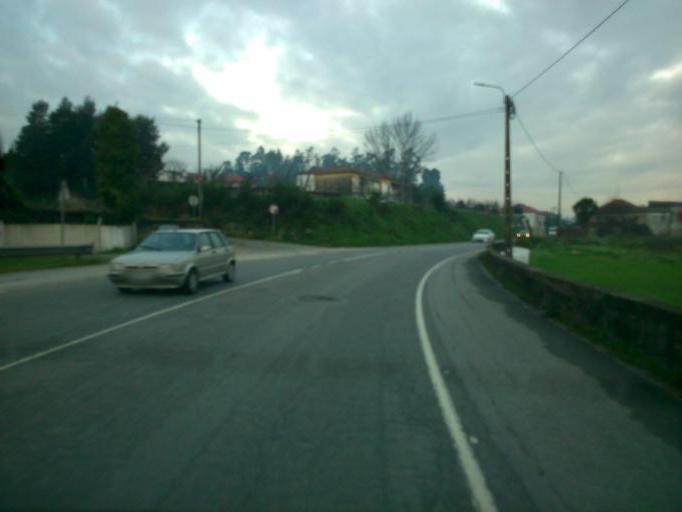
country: PT
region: Braga
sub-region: Barcelos
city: Barcelos
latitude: 41.5076
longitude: -8.5805
